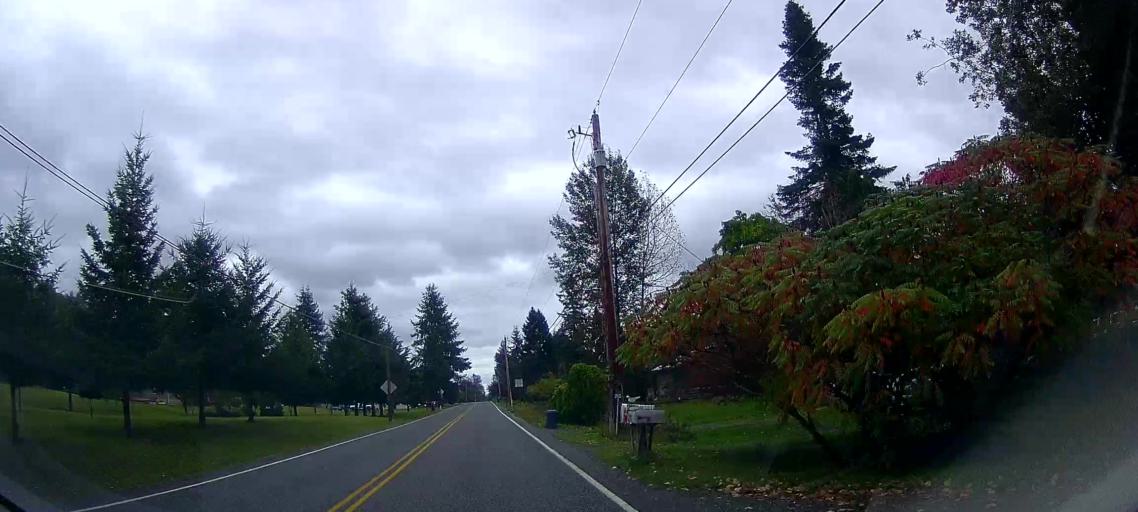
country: US
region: Washington
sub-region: Skagit County
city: Sedro-Woolley
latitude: 48.5266
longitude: -122.1041
